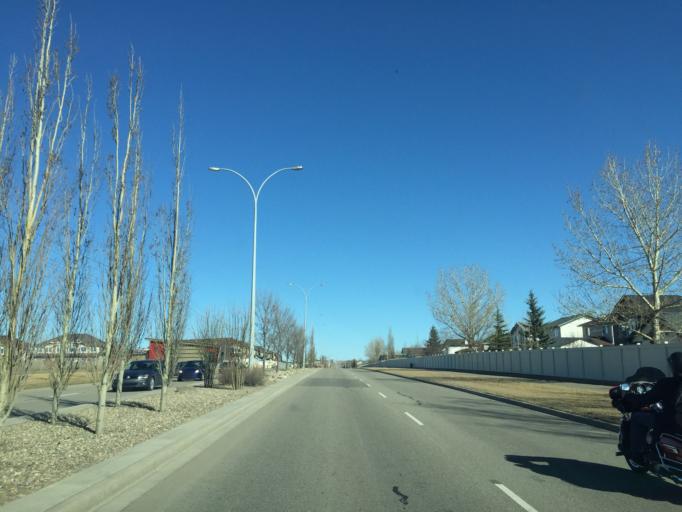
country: CA
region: Alberta
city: Airdrie
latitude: 51.3000
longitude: -114.0394
